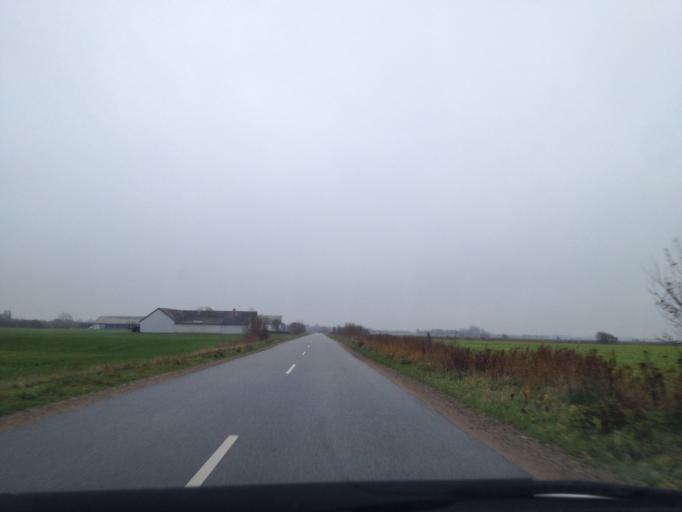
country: DK
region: South Denmark
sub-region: Tonder Kommune
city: Sherrebek
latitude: 55.0974
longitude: 8.7267
